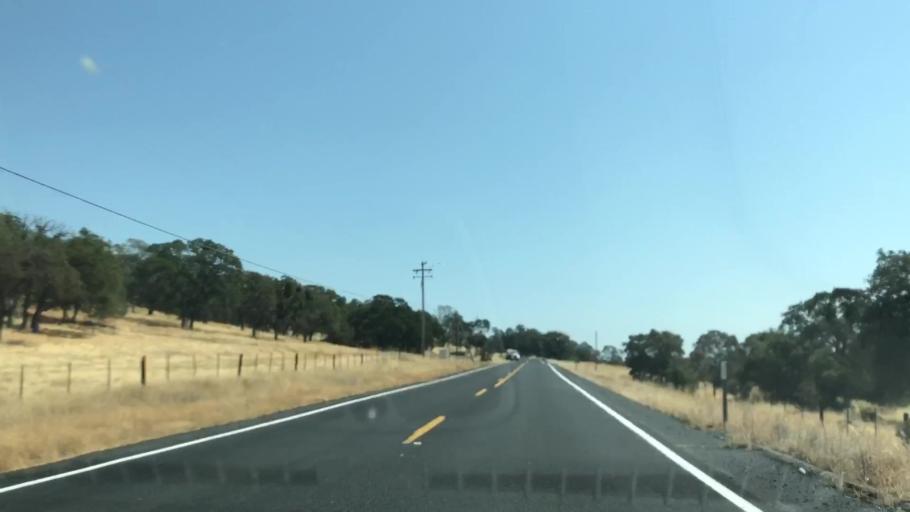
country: US
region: California
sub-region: Calaveras County
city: Copperopolis
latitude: 37.8892
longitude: -120.5436
